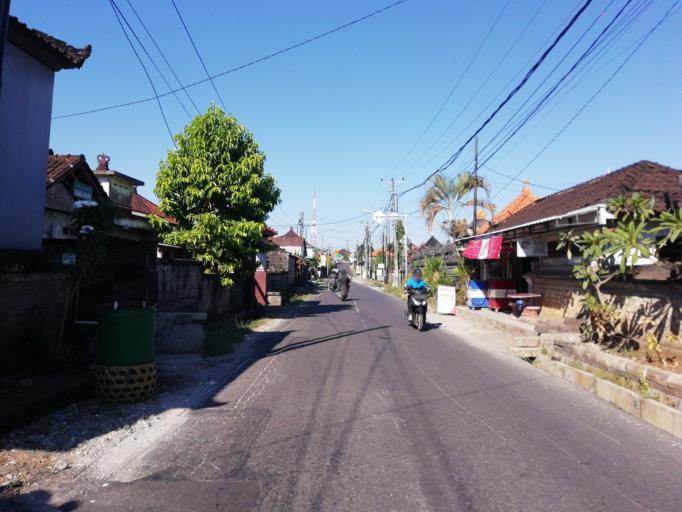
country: ID
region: Bali
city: Jimbaran
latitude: -8.8288
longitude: 115.1758
